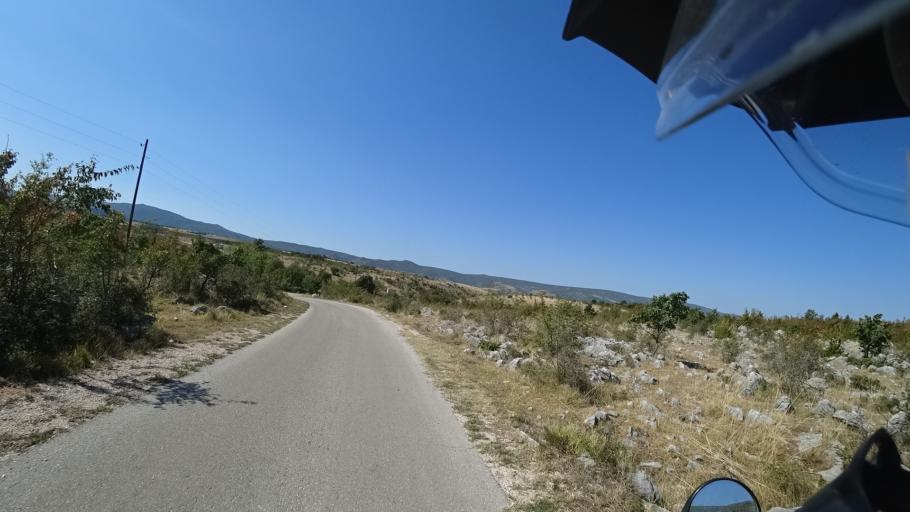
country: HR
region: Sibensko-Kniniska
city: Drnis
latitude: 43.8070
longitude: 16.3378
